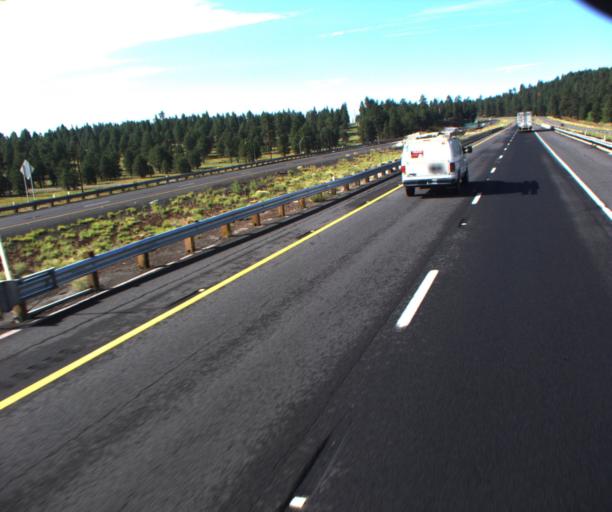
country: US
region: Arizona
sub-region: Coconino County
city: Kachina Village
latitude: 35.0917
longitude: -111.6856
